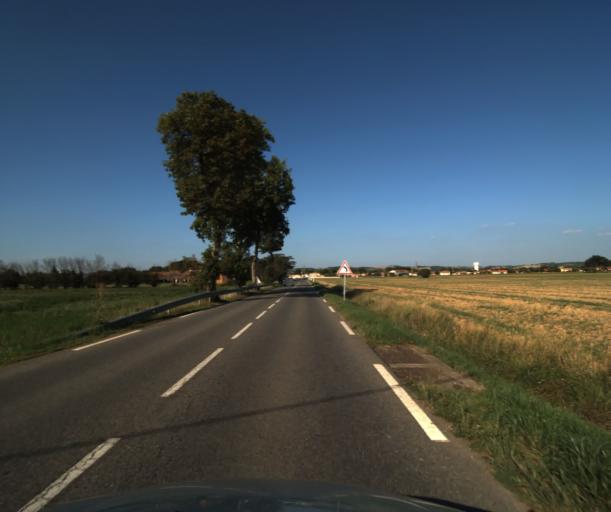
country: FR
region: Midi-Pyrenees
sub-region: Departement de la Haute-Garonne
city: Labarthe-sur-Leze
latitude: 43.4496
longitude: 1.3889
